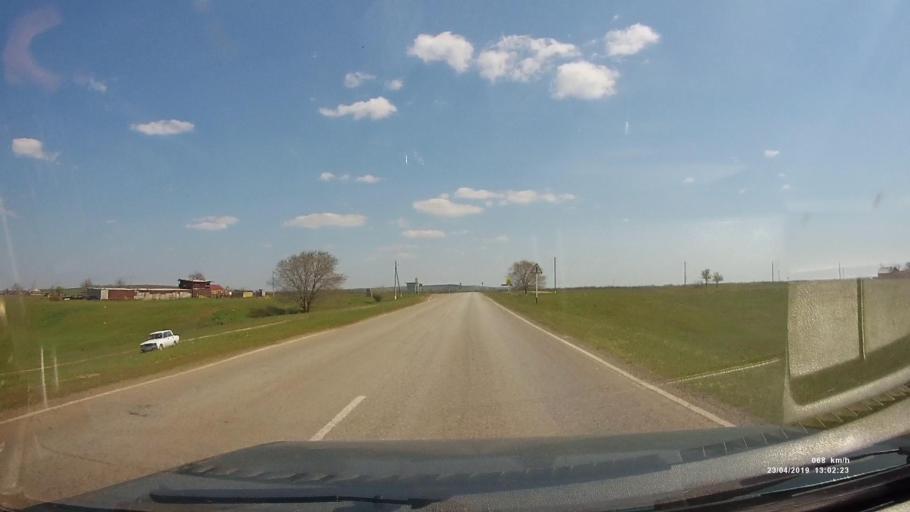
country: RU
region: Kalmykiya
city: Yashalta
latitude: 46.6007
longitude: 42.6688
